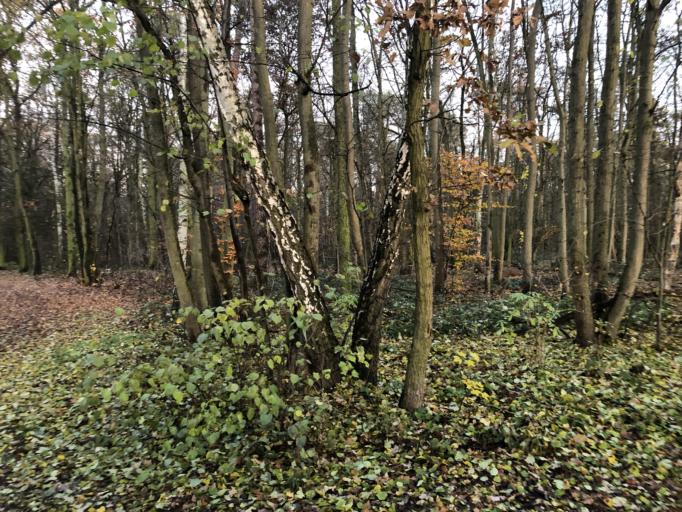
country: DE
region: Saxony-Anhalt
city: Lieskau
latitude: 51.4942
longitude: 11.8774
